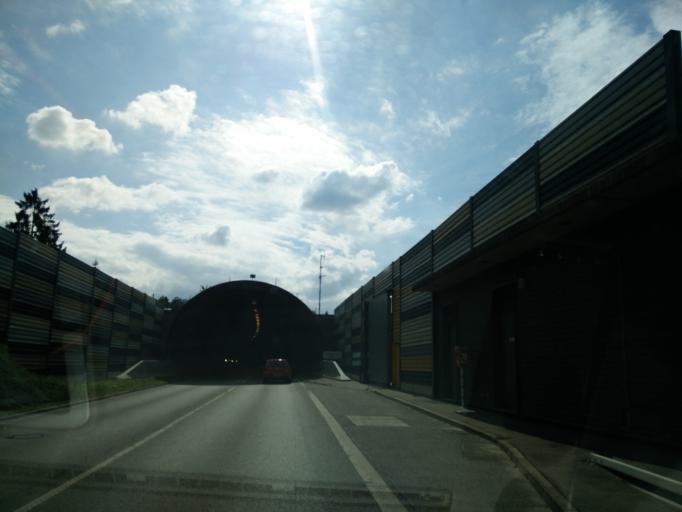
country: DE
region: Baden-Wuerttemberg
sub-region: Tuebingen Region
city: Pfullingen
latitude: 48.4719
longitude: 9.2316
